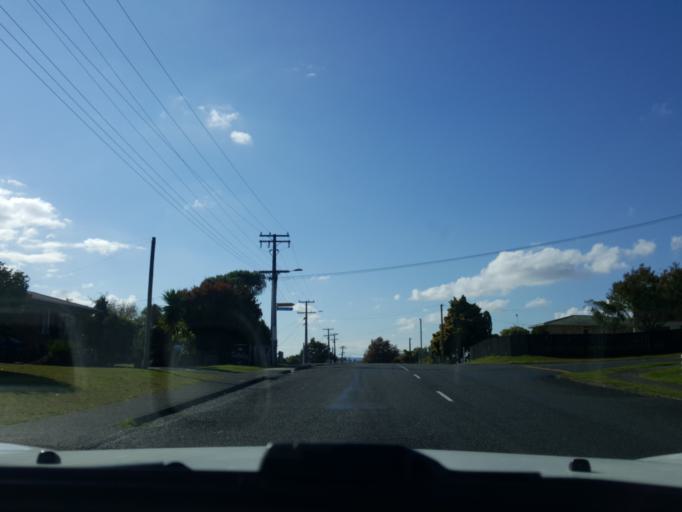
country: NZ
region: Waikato
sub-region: Waikato District
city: Ngaruawahia
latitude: -37.5437
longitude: 175.1698
